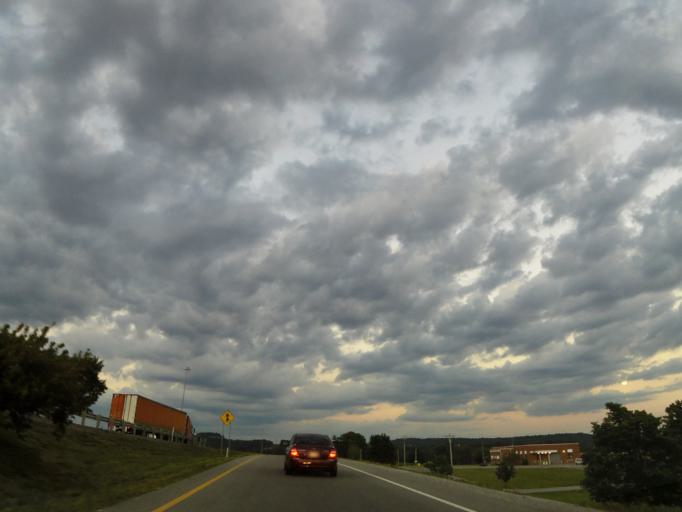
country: US
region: Tennessee
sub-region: Putnam County
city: Cookeville
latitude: 36.1350
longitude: -85.5022
